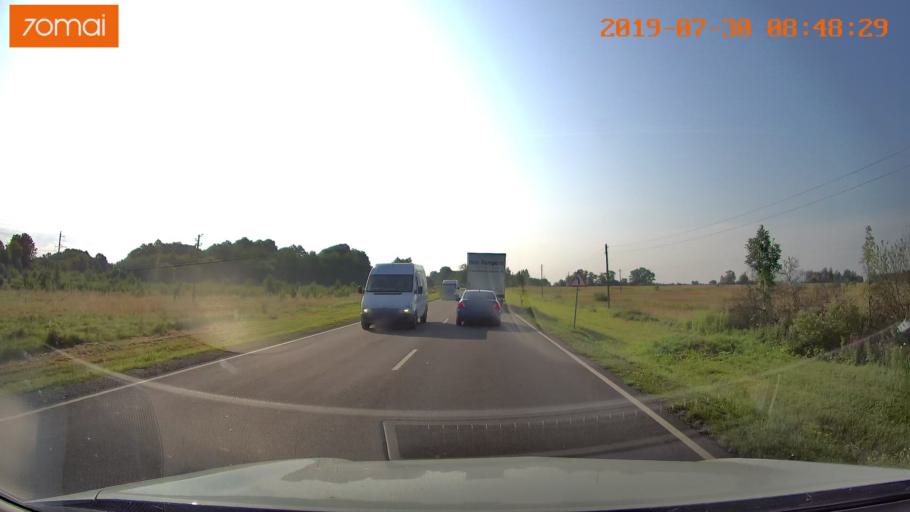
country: RU
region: Kaliningrad
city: Chernyakhovsk
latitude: 54.6174
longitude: 21.9063
